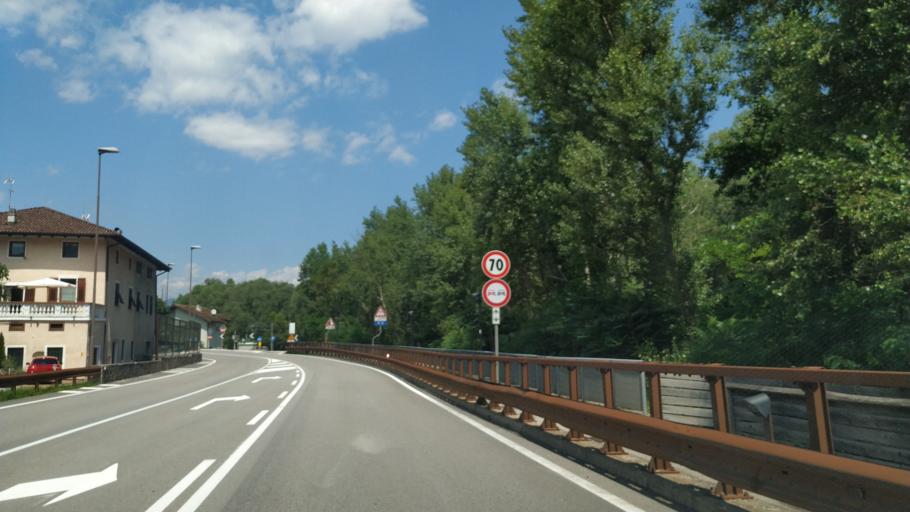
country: IT
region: Trentino-Alto Adige
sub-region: Provincia di Trento
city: Spormaggiore
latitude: 46.2427
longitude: 11.0588
